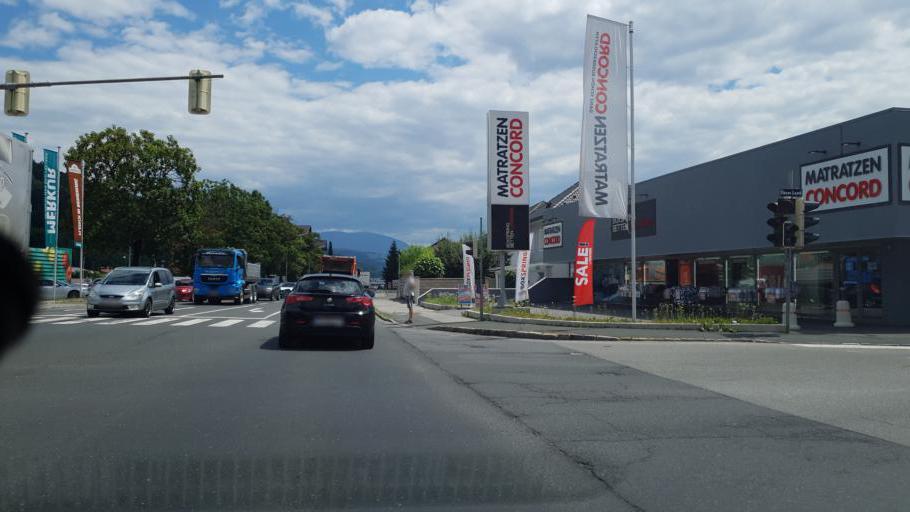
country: AT
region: Carinthia
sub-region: Politischer Bezirk Spittal an der Drau
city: Spittal an der Drau
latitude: 46.7914
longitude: 13.5117
